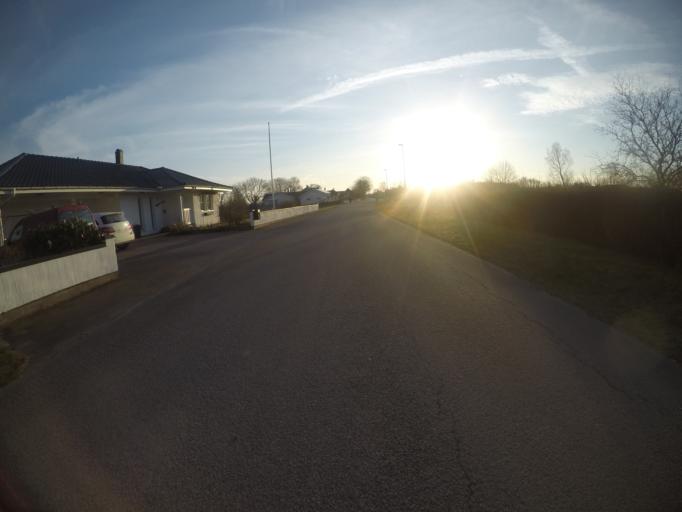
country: SE
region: Halland
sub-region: Laholms Kommun
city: Laholm
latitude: 56.5039
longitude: 13.0159
